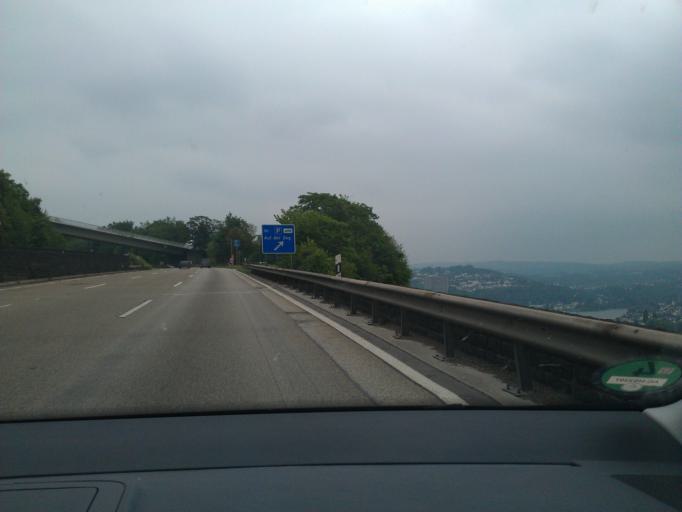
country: DE
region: Rheinland-Pfalz
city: Weitersburg
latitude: 50.4077
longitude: 7.5976
